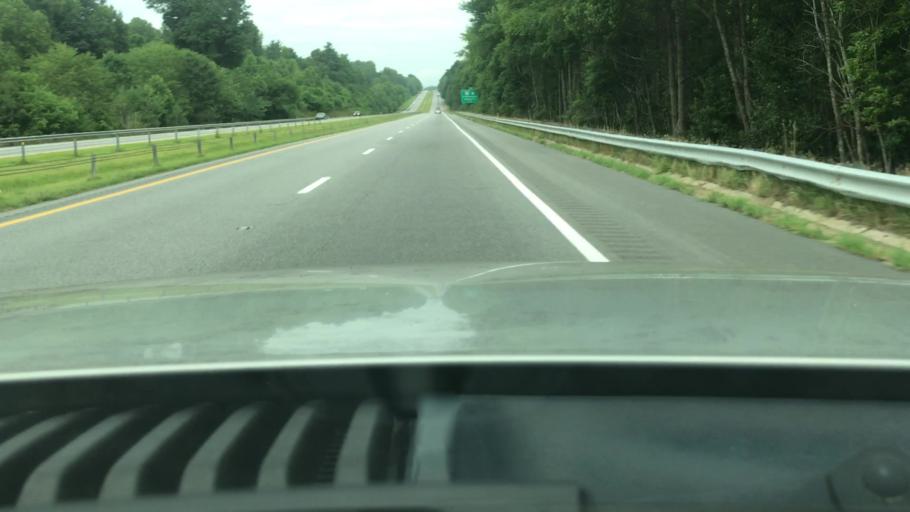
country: US
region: North Carolina
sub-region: Wilkes County
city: North Wilkesboro
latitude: 36.1394
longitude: -81.0792
